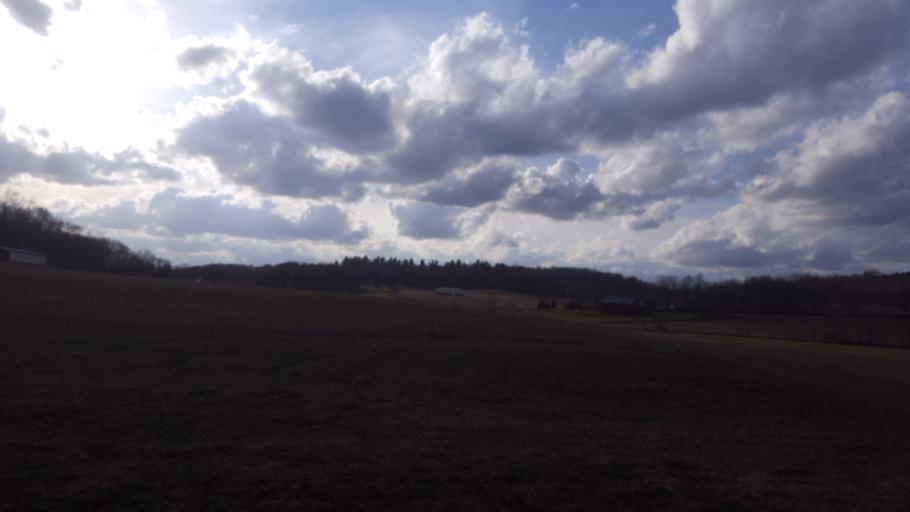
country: US
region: Ohio
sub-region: Sandusky County
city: Bellville
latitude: 40.5737
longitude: -82.4375
